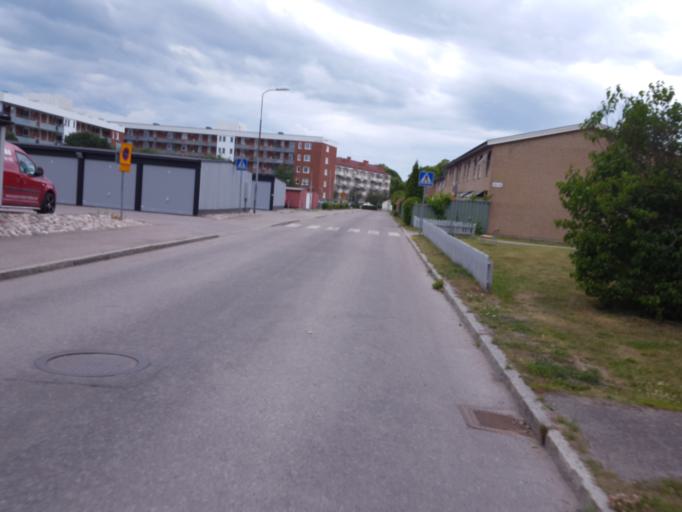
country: SE
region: Uppsala
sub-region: Uppsala Kommun
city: Uppsala
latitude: 59.8638
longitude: 17.6810
